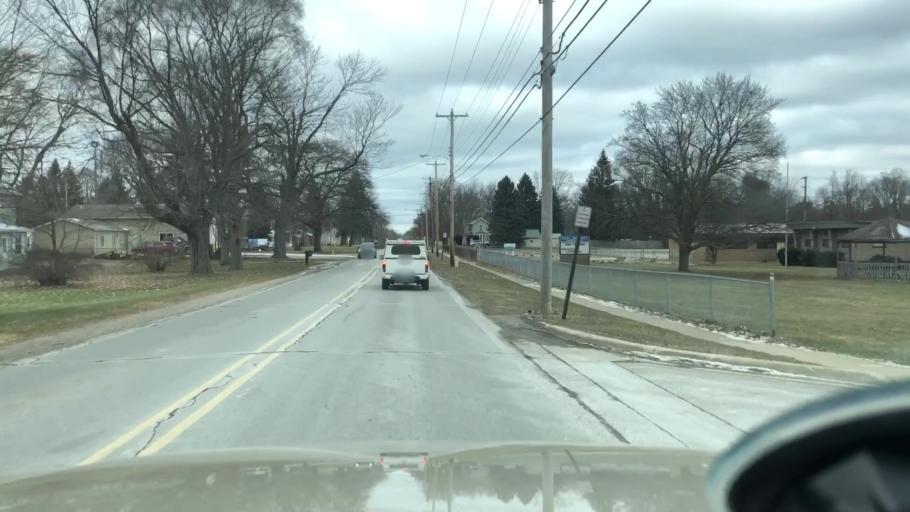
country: US
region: Michigan
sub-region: Jackson County
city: Jackson
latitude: 42.2594
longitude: -84.3649
